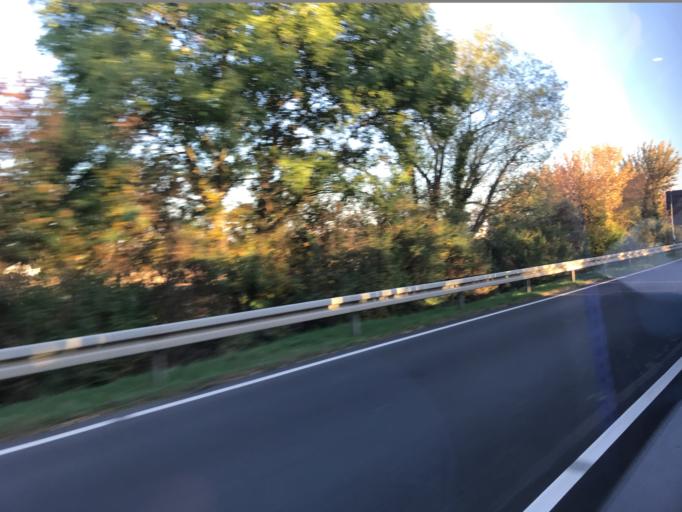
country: DE
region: Hesse
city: Liederbach
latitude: 50.1258
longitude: 8.4736
